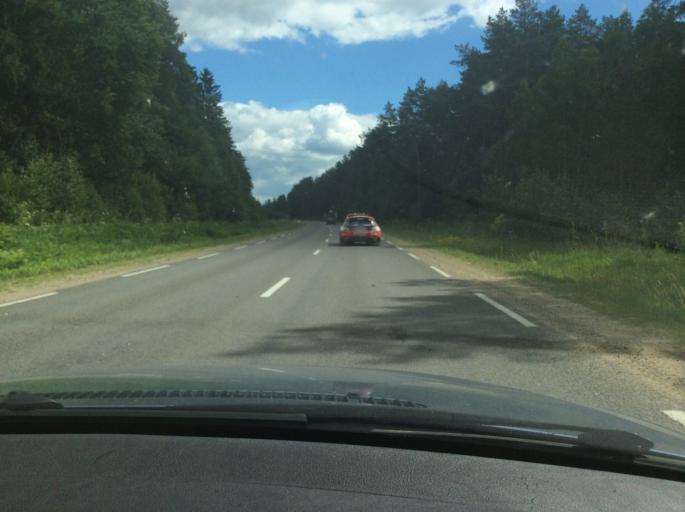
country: LT
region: Alytaus apskritis
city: Druskininkai
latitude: 54.0367
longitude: 23.9528
